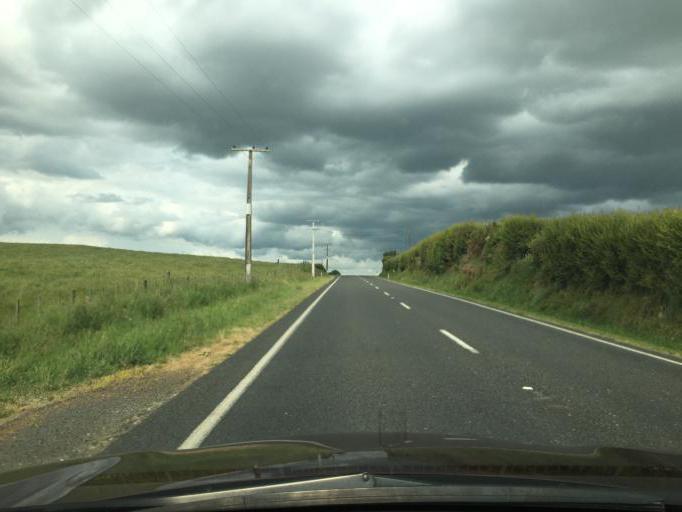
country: NZ
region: Waikato
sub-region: Waipa District
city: Cambridge
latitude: -38.0027
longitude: 175.3864
